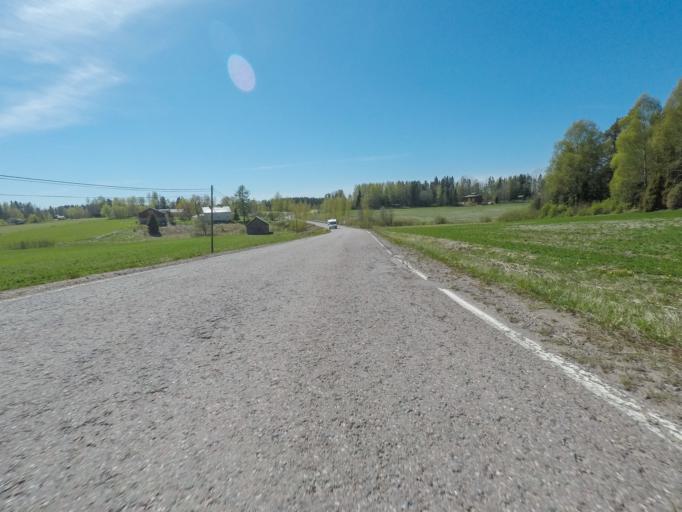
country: FI
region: Uusimaa
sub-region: Helsinki
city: Kaerkoelae
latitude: 60.5847
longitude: 23.7961
